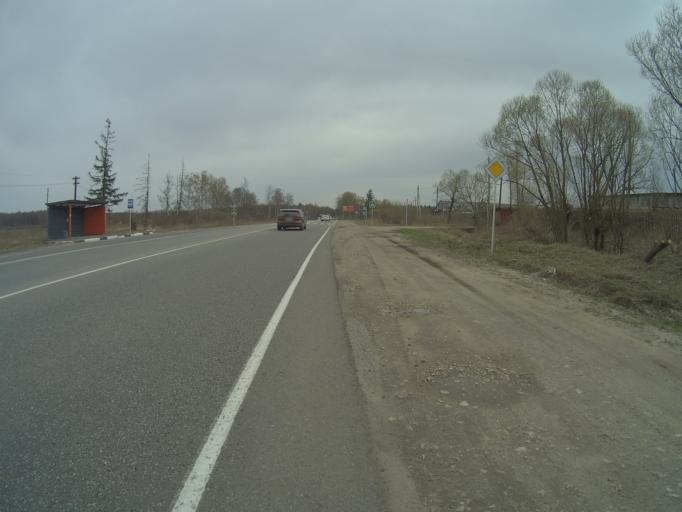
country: RU
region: Vladimir
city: Kommunar
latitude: 56.0385
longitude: 40.5519
